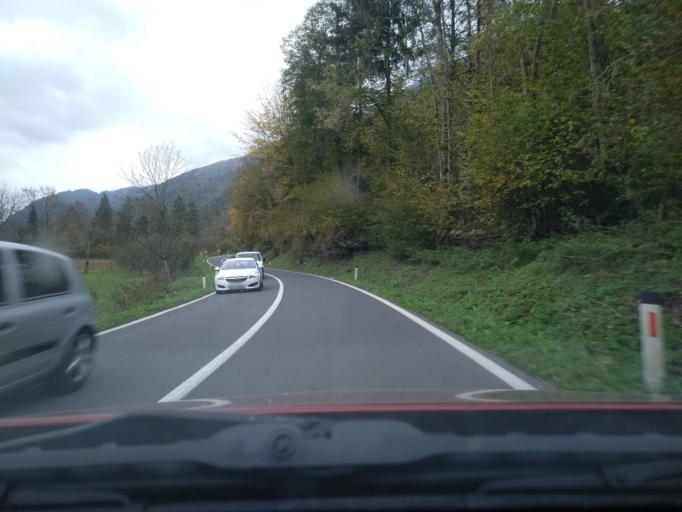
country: SI
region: Kobarid
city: Kobarid
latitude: 46.2192
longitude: 13.6081
